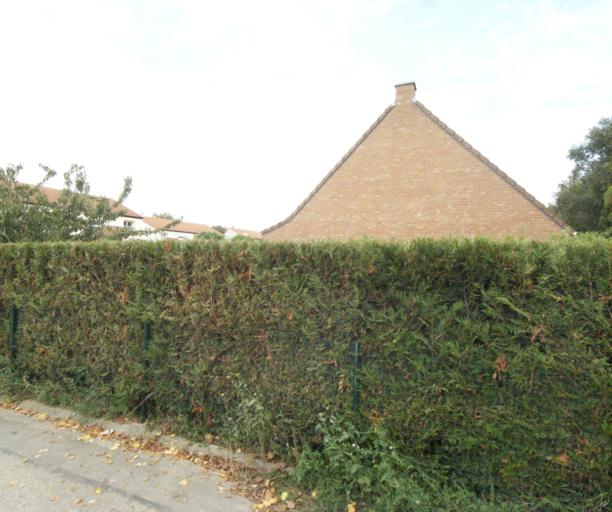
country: FR
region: Nord-Pas-de-Calais
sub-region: Departement du Nord
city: Salome
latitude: 50.5295
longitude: 2.8407
